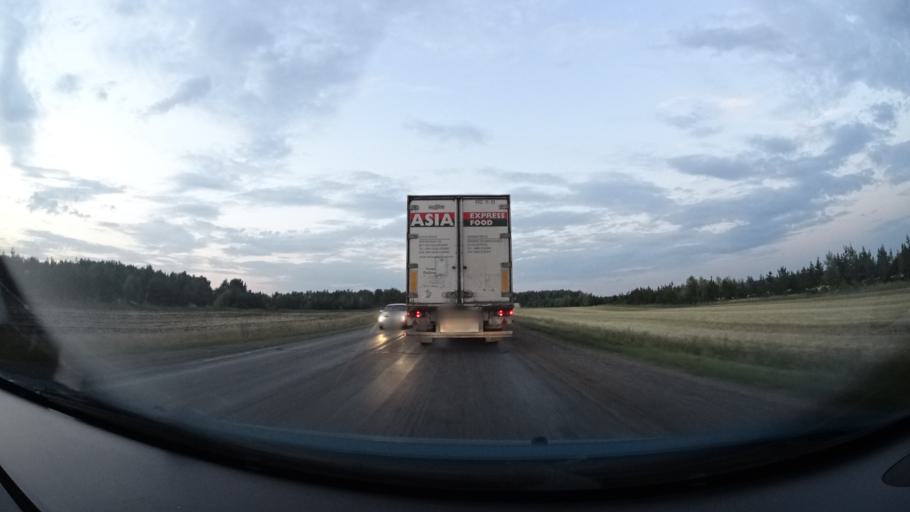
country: RU
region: Tatarstan
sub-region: Bavlinskiy Rayon
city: Bavly
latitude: 54.2829
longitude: 52.9923
